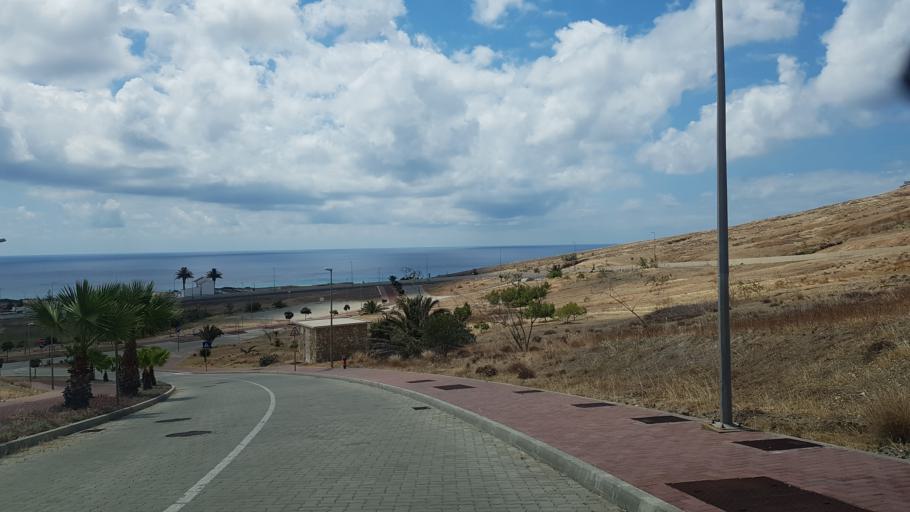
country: PT
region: Madeira
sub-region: Porto Santo
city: Vila de Porto Santo
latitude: 33.0478
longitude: -16.3643
